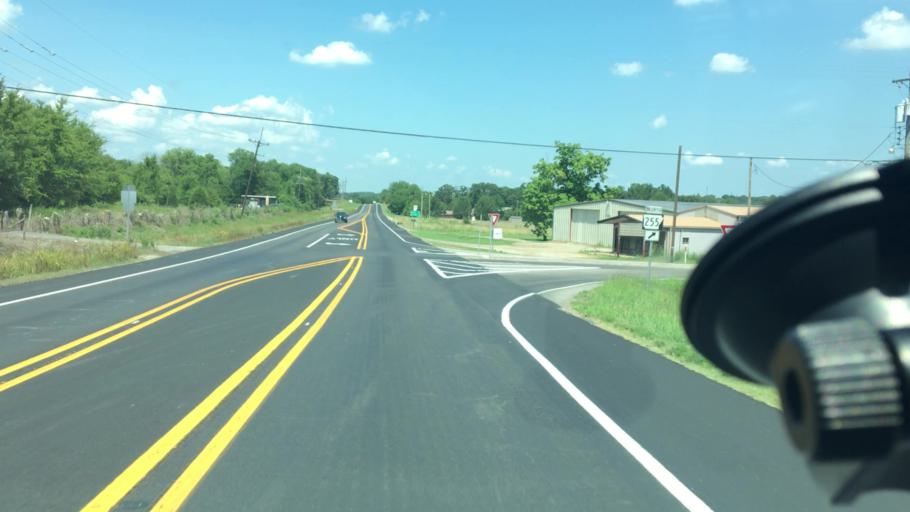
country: US
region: Arkansas
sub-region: Sebastian County
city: Lavaca
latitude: 35.3019
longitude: -94.1622
